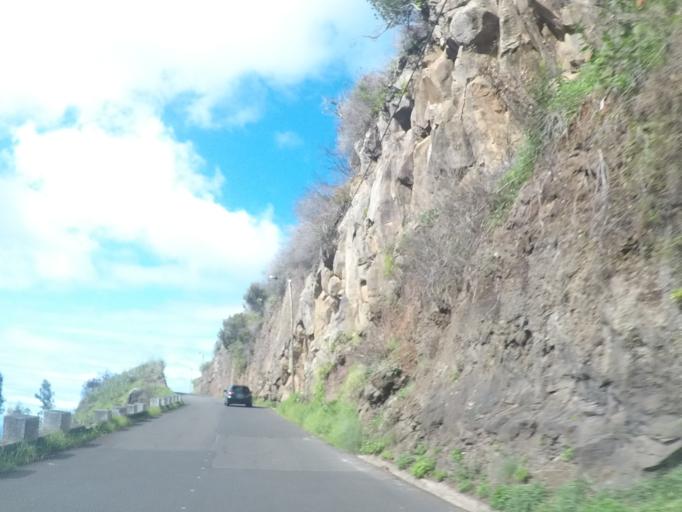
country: PT
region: Madeira
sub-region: Calheta
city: Faja da Ovelha
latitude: 32.8132
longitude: -17.2399
